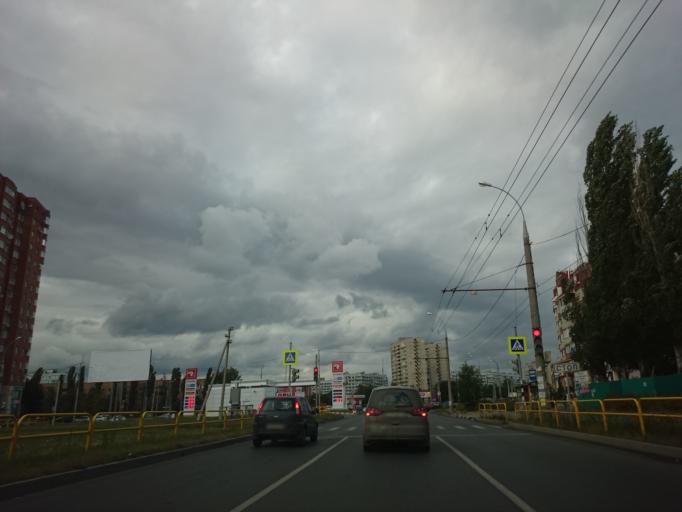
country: RU
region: Samara
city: Tol'yatti
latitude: 53.5153
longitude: 49.3085
